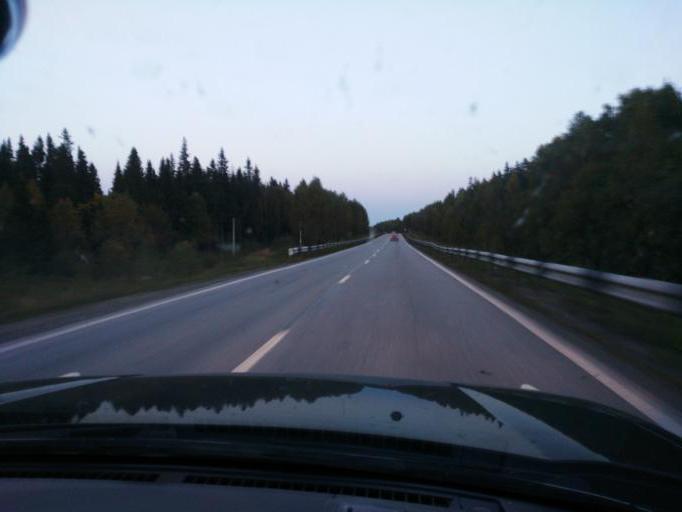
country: RU
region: Perm
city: Verkhnechusovskiye Gorodki
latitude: 58.2500
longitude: 57.0143
